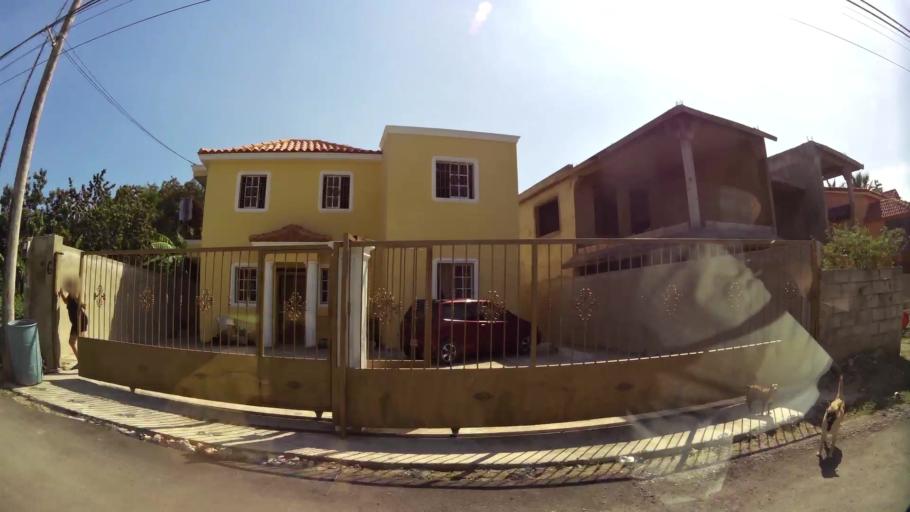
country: DO
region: Santo Domingo
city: Santo Domingo Oeste
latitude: 18.4746
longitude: -70.0041
